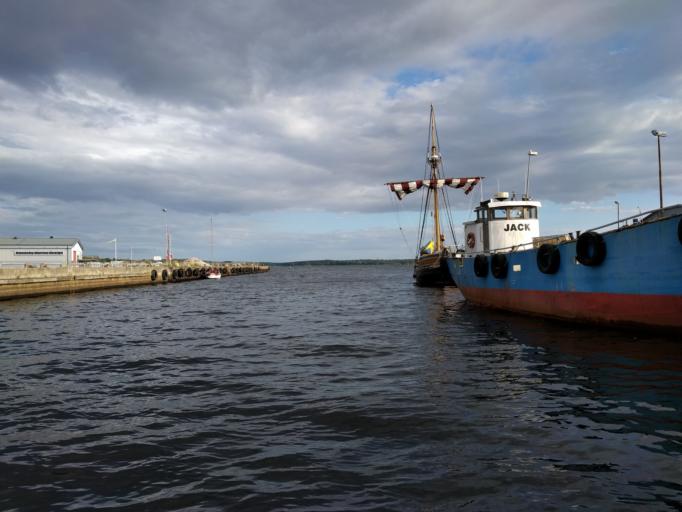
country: SE
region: Blekinge
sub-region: Ronneby Kommun
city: Ronneby
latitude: 56.1759
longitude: 15.3009
